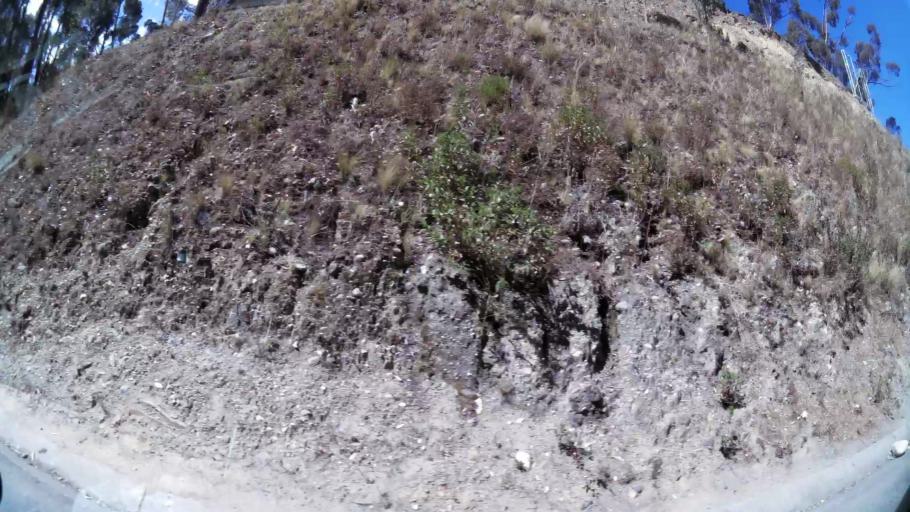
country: BO
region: La Paz
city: La Paz
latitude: -16.4717
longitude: -68.1597
